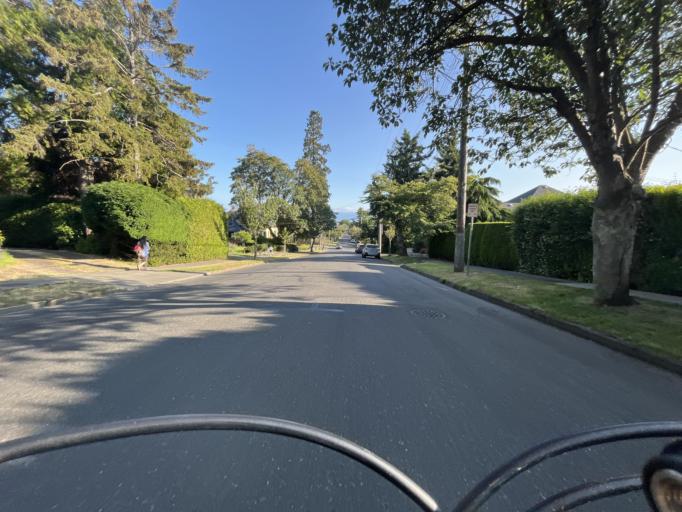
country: CA
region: British Columbia
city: Victoria
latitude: 48.4197
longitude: -123.3478
